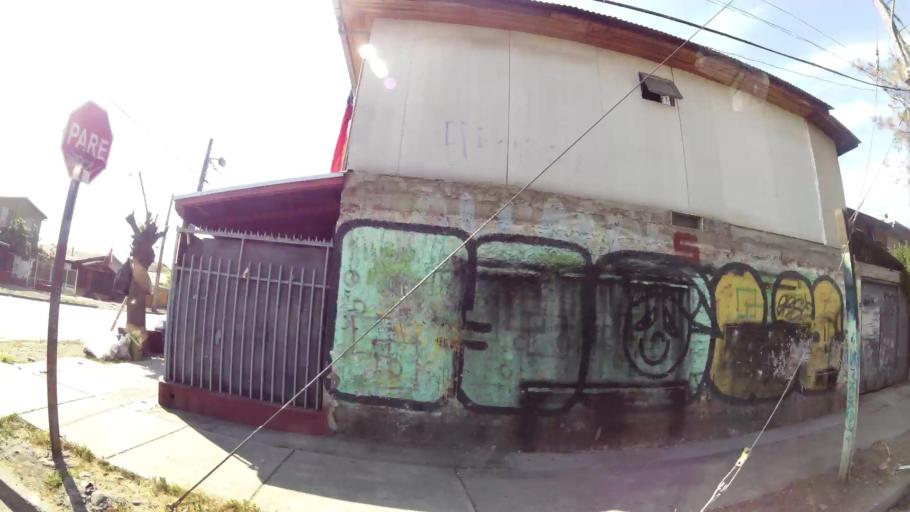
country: CL
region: Santiago Metropolitan
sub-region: Provincia de Santiago
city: La Pintana
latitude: -33.5600
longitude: -70.6543
